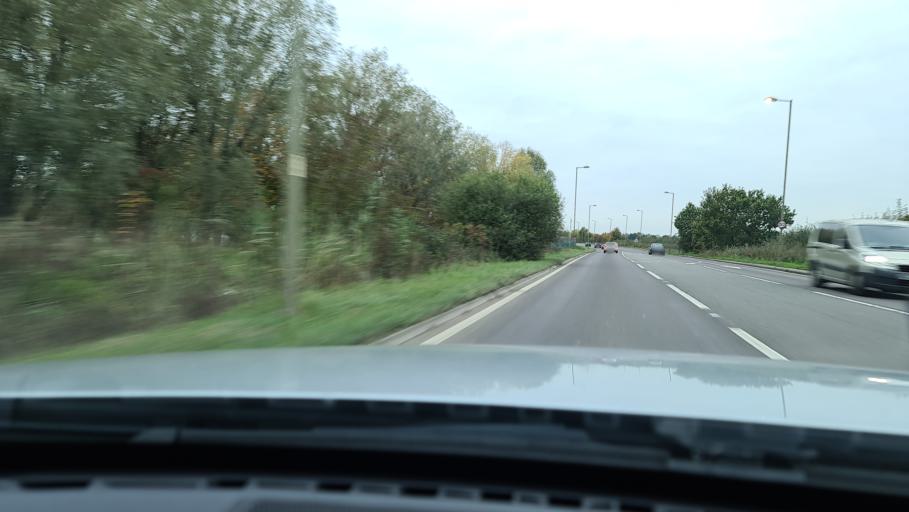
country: GB
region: England
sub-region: Oxfordshire
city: Bicester
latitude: 51.8824
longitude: -1.1347
